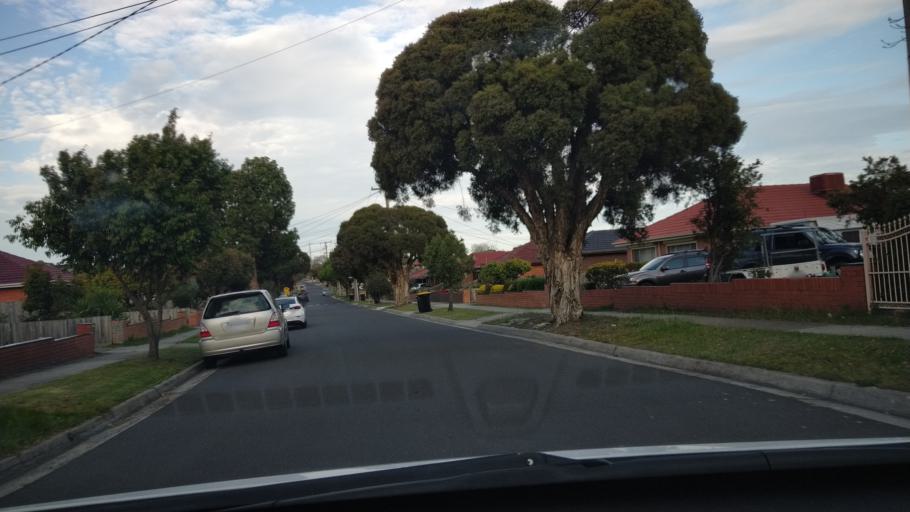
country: AU
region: Victoria
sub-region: Greater Dandenong
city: Springvale South
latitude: -37.9643
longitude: 145.1552
